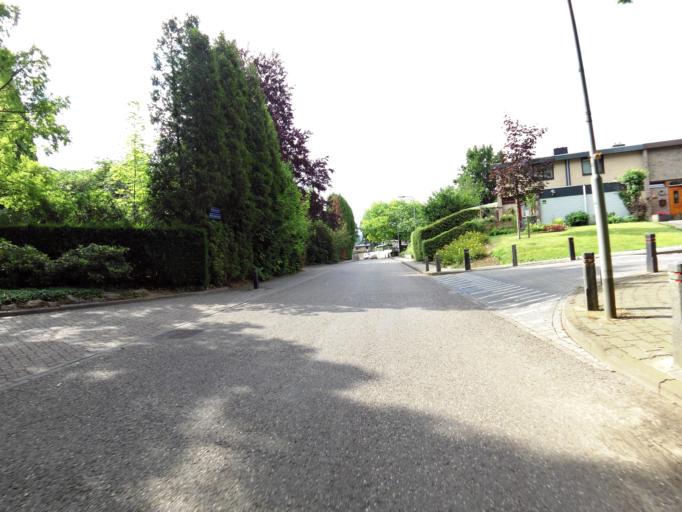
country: NL
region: Limburg
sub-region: Valkenburg aan de Geul
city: Valkenburg
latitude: 50.8733
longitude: 5.8325
